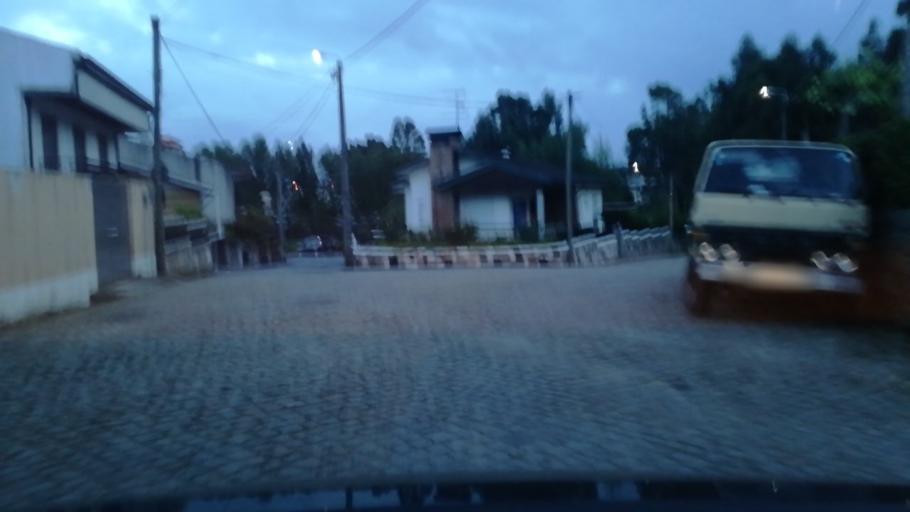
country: PT
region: Porto
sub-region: Maia
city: Anta
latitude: 41.2525
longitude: -8.6266
